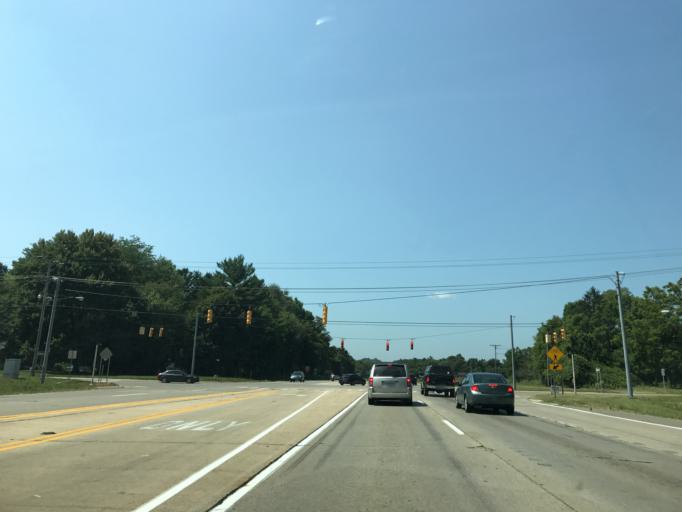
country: US
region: Michigan
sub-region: Berrien County
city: Niles
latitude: 41.8011
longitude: -86.2538
